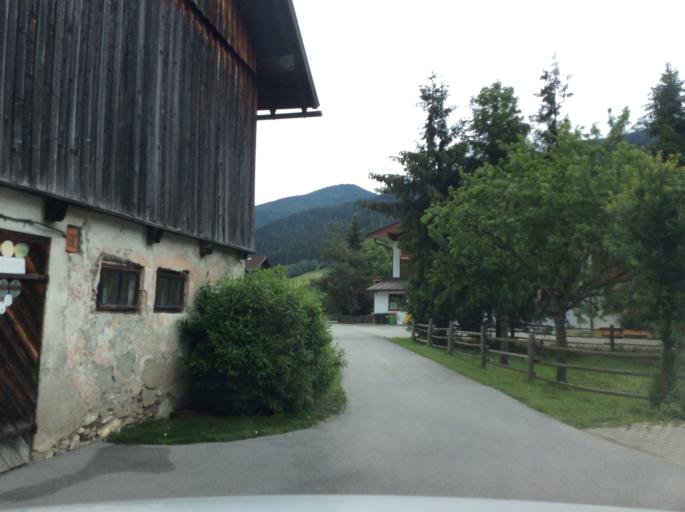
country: AT
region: Styria
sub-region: Politischer Bezirk Liezen
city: Schladming
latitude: 47.4045
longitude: 13.7093
